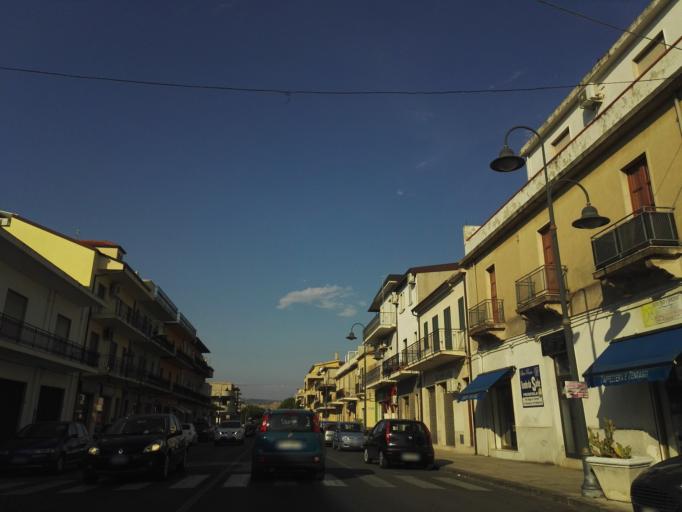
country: IT
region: Calabria
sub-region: Provincia di Reggio Calabria
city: Marina di Gioiosa Ionica
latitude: 38.3016
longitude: 16.3322
